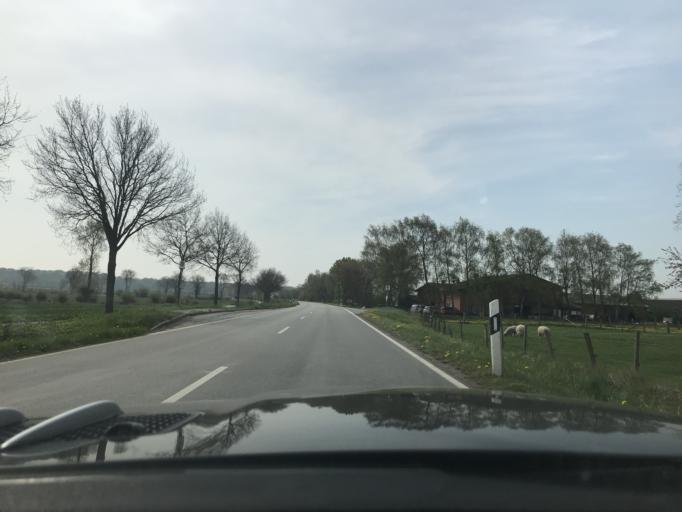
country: DE
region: Schleswig-Holstein
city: Grube
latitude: 54.2173
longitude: 11.0348
